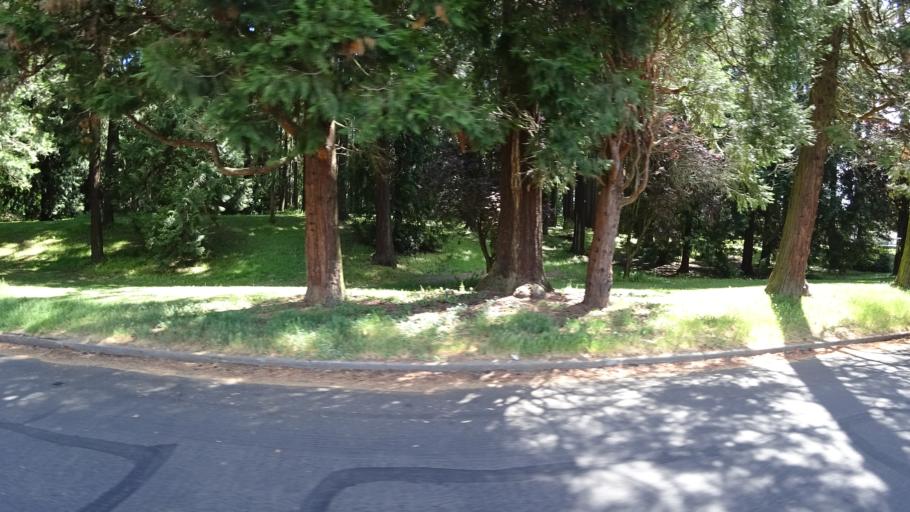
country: US
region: Oregon
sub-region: Washington County
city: West Haven
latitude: 45.5997
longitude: -122.7559
